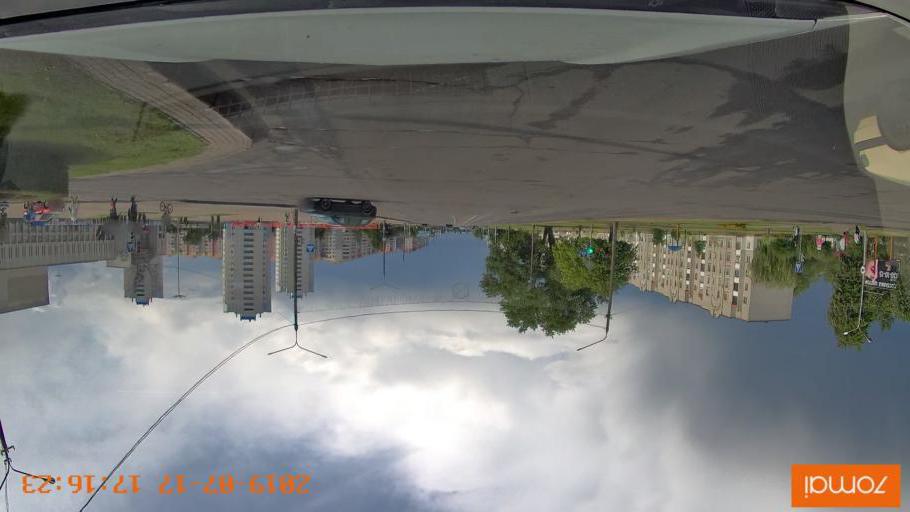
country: BY
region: Mogilev
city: Babruysk
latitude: 53.1683
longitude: 29.1929
